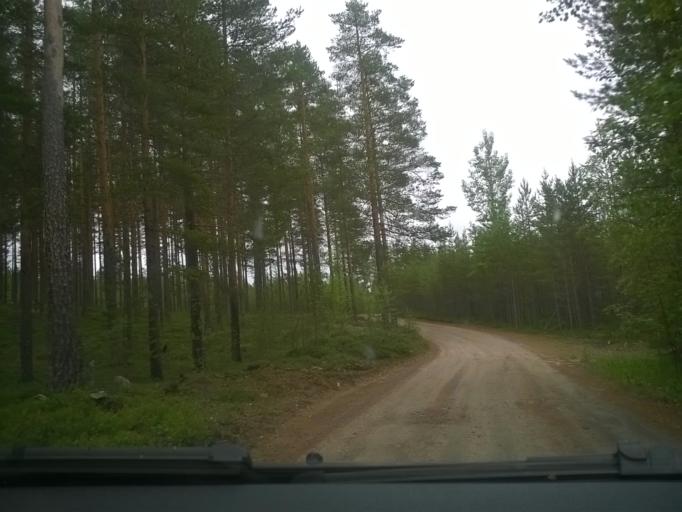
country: FI
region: Kainuu
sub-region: Kehys-Kainuu
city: Kuhmo
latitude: 64.1476
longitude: 29.4072
